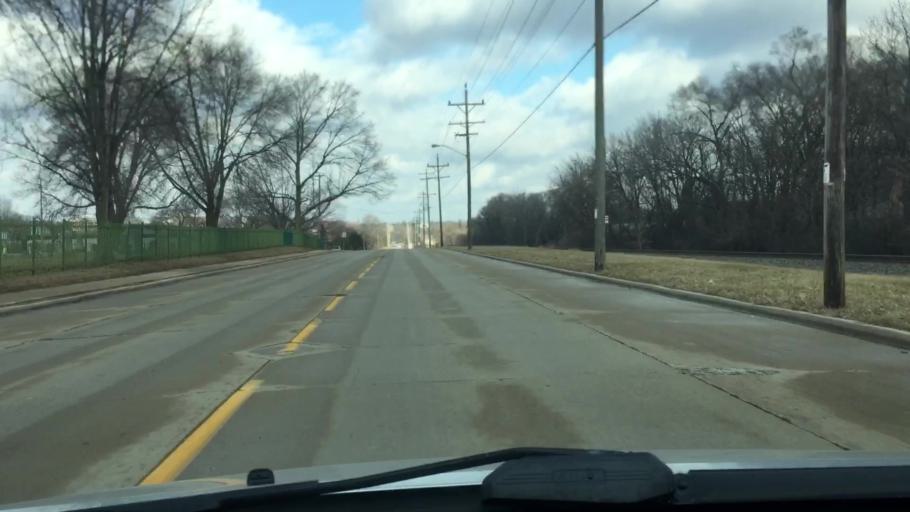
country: US
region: Wisconsin
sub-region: Waukesha County
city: Waukesha
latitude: 42.9956
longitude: -88.2369
